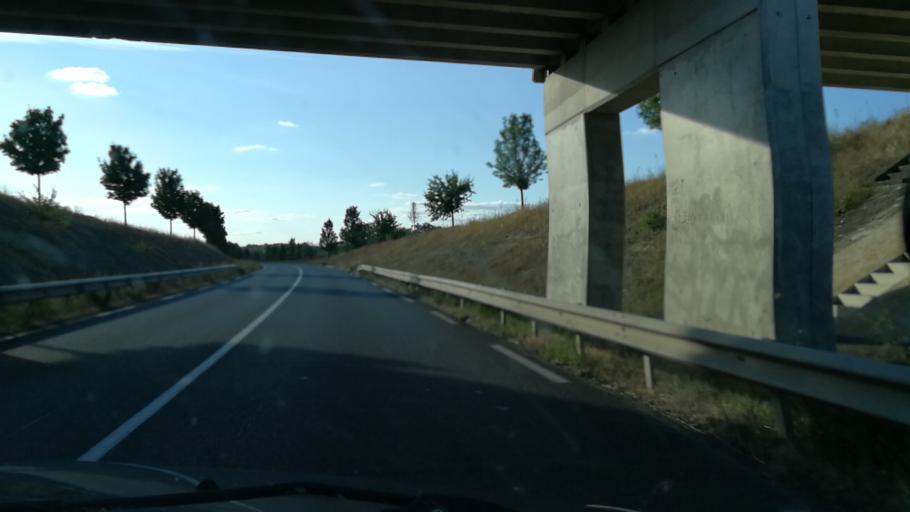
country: FR
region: Centre
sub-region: Departement d'Indre-et-Loire
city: Sainte-Maure-de-Touraine
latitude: 47.1038
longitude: 0.6038
